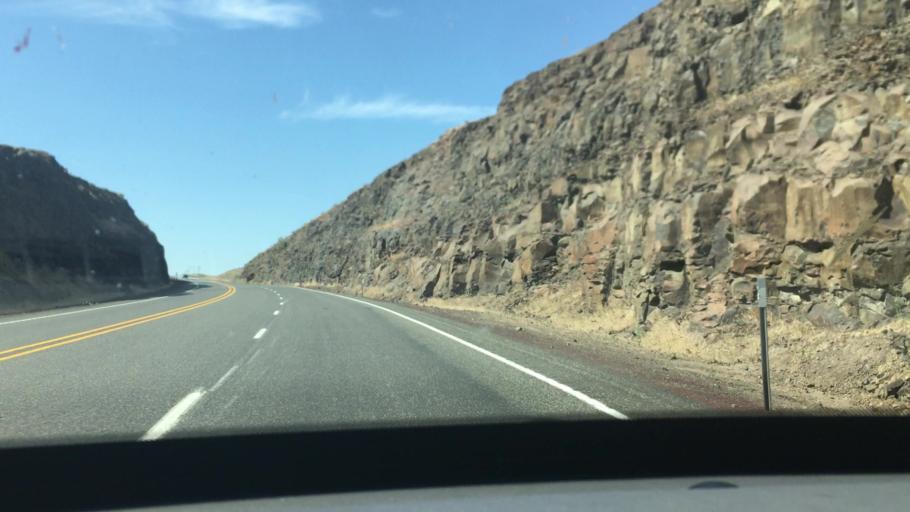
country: US
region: Oregon
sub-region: Sherman County
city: Moro
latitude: 45.5148
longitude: -120.6836
